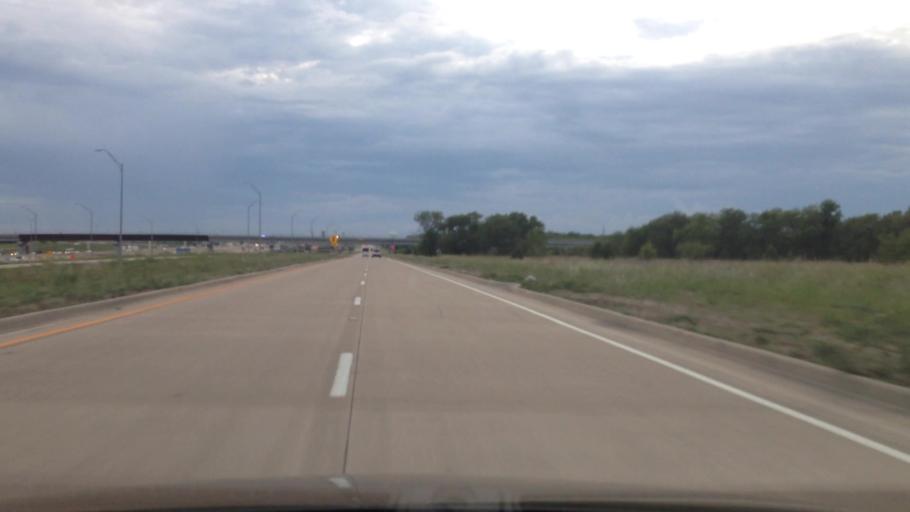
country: US
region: Texas
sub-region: Tarrant County
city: Grapevine
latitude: 32.9323
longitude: -97.0465
